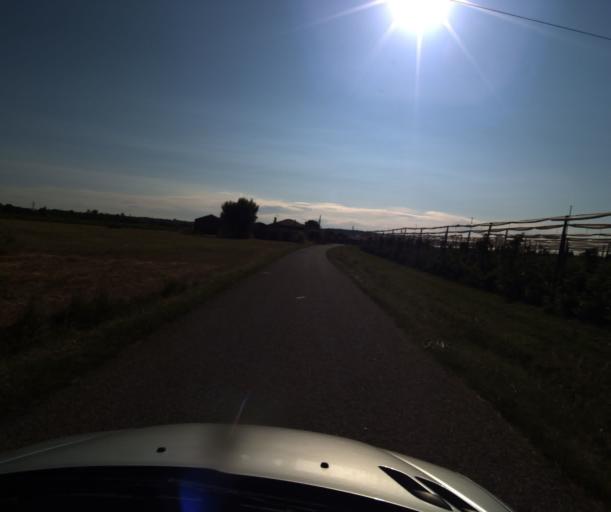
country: FR
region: Midi-Pyrenees
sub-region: Departement du Tarn-et-Garonne
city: Bressols
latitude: 43.9685
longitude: 1.3240
